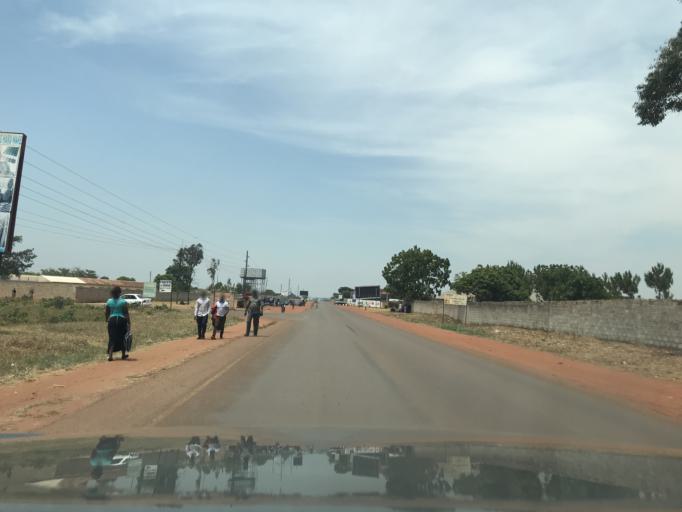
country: ZM
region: Northern
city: Kasama
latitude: -10.2073
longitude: 31.1737
